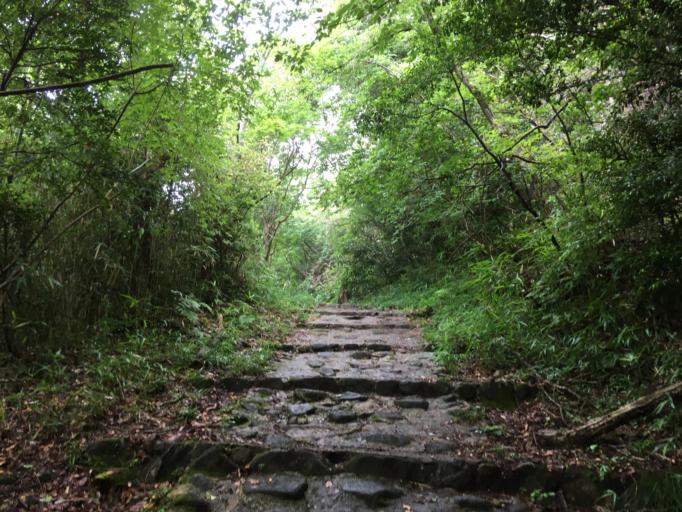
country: JP
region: Nara
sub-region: Ikoma-shi
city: Ikoma
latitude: 34.6831
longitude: 135.6844
